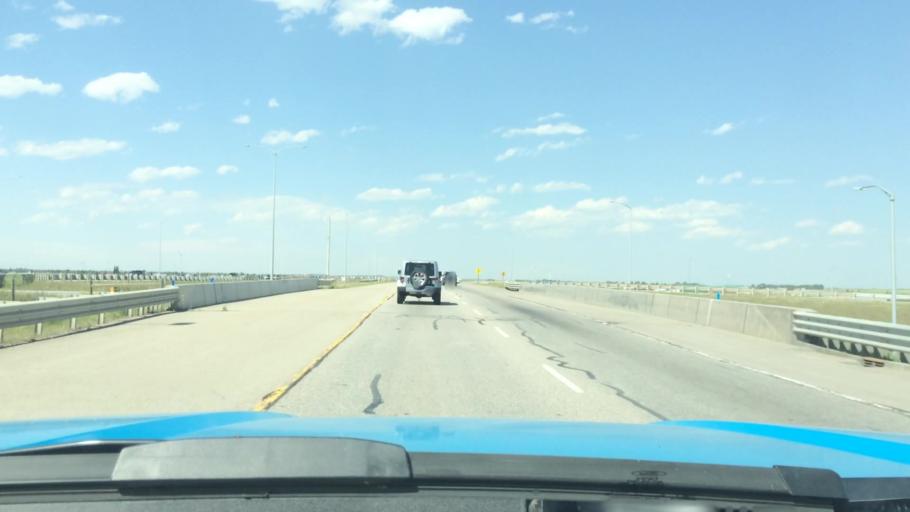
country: CA
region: Alberta
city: Chestermere
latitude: 51.0643
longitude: -113.9202
